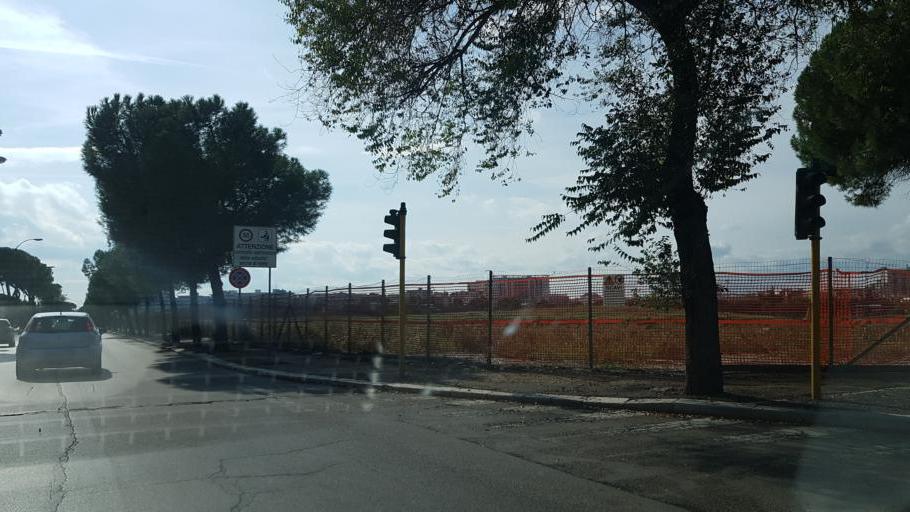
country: IT
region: Apulia
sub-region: Provincia di Foggia
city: Foggia
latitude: 41.4611
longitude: 15.5644
